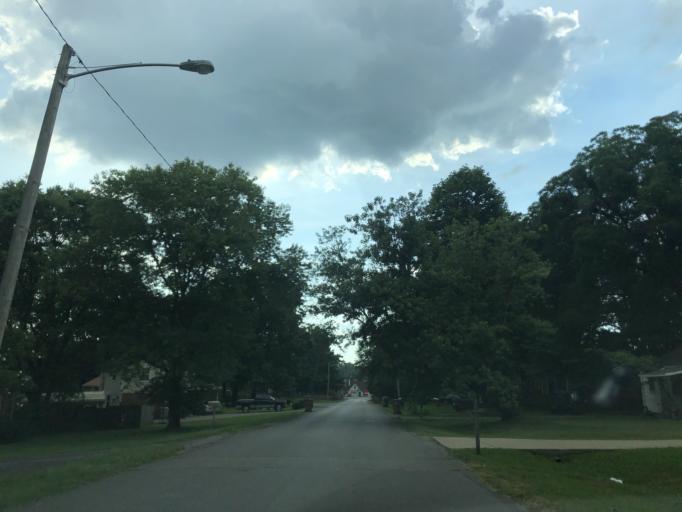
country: US
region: Tennessee
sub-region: Davidson County
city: Lakewood
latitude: 36.1677
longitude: -86.6772
